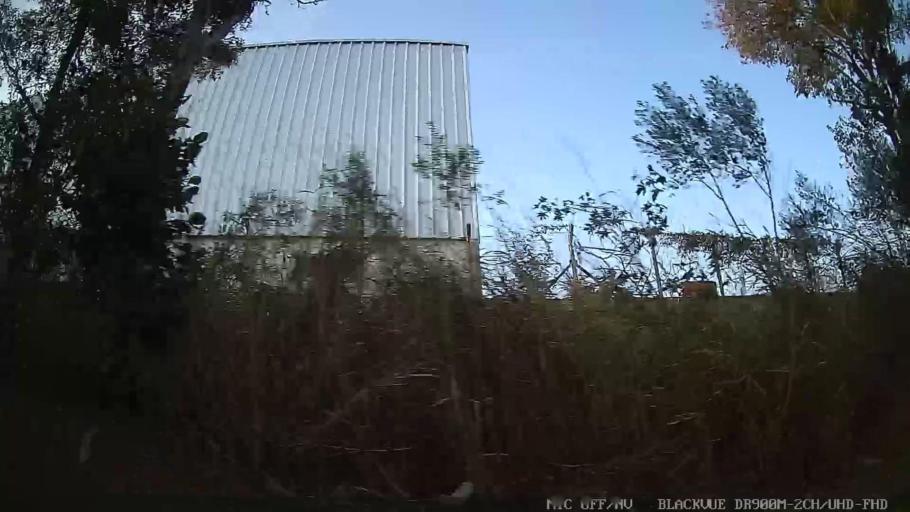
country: BR
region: Sao Paulo
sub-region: Itupeva
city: Itupeva
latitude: -23.2380
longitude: -47.0645
